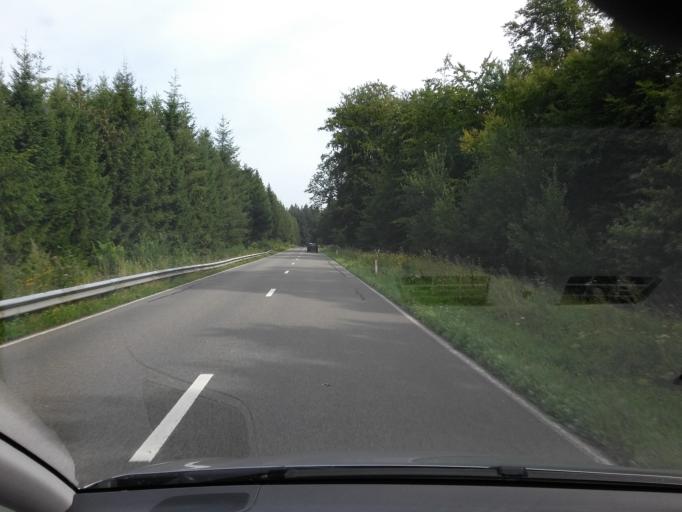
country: BE
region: Wallonia
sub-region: Province du Luxembourg
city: Chiny
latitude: 49.7705
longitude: 5.3241
